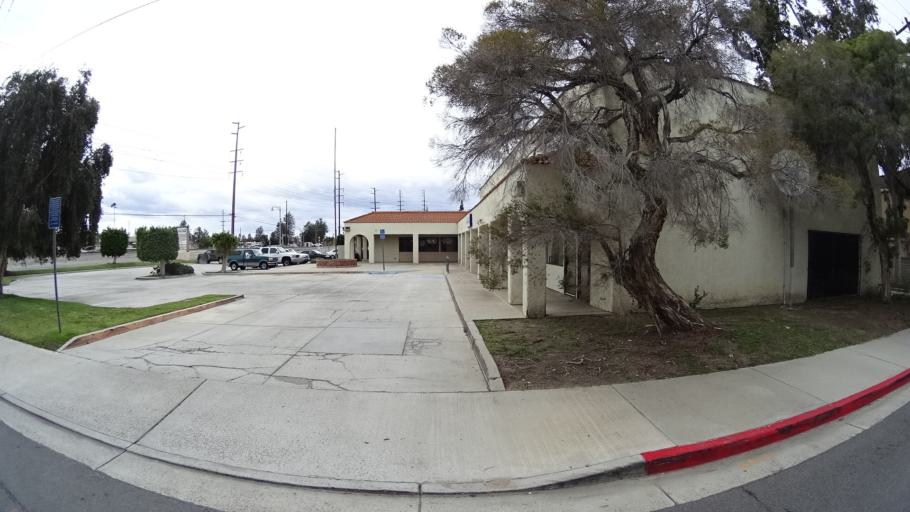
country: US
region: California
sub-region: Orange County
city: Yorba Linda
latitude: 33.8685
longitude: -117.8290
